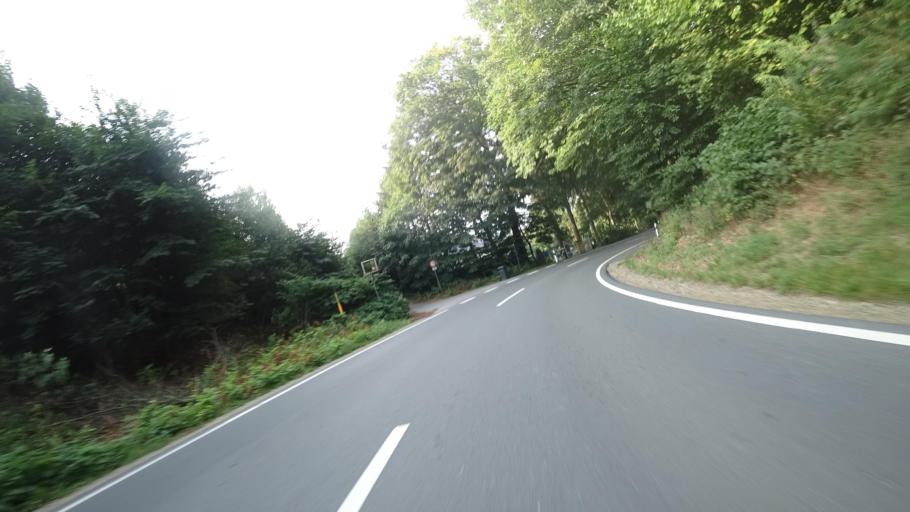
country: DE
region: North Rhine-Westphalia
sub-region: Regierungsbezirk Detmold
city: Steinhagen
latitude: 52.0208
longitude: 8.4570
